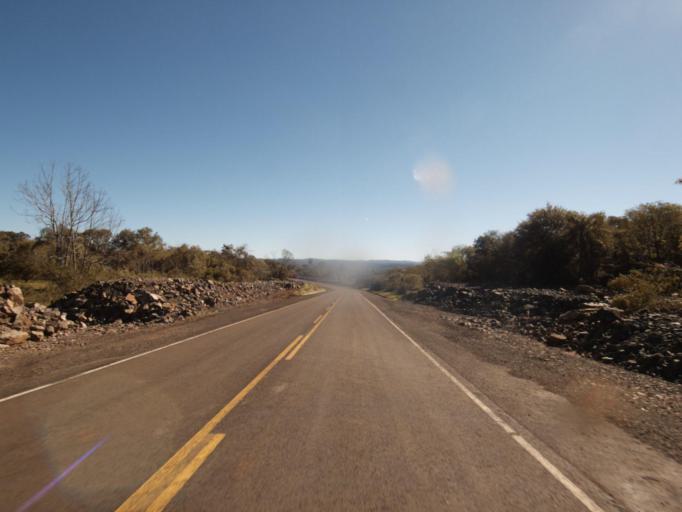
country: AR
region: Misiones
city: Bernardo de Irigoyen
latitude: -26.6143
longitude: -53.7104
